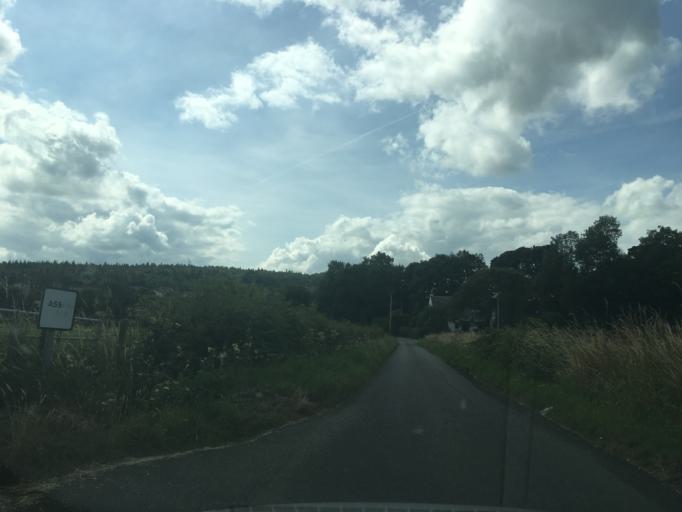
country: GB
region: Scotland
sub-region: Stirling
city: Stirling
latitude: 56.1151
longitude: -3.9756
